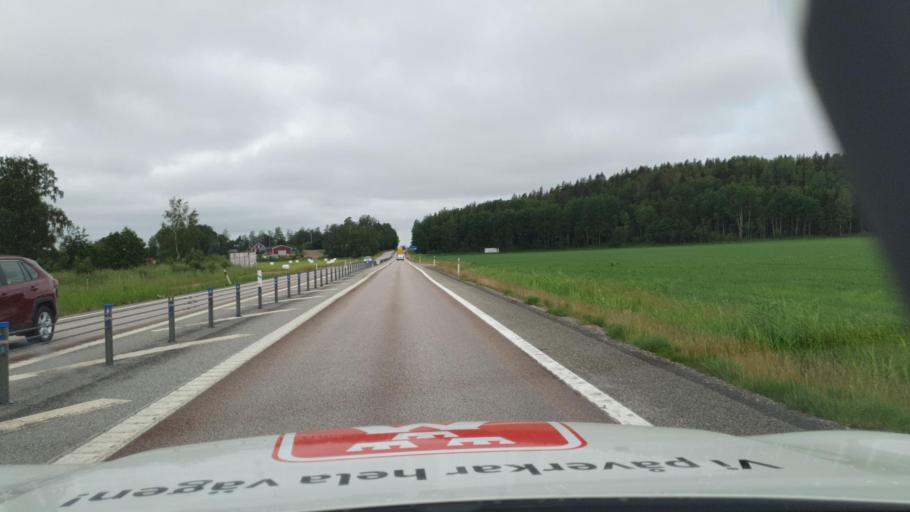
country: SE
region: Vaermland
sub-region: Kristinehamns Kommun
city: Kristinehamn
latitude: 59.3751
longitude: 13.9656
